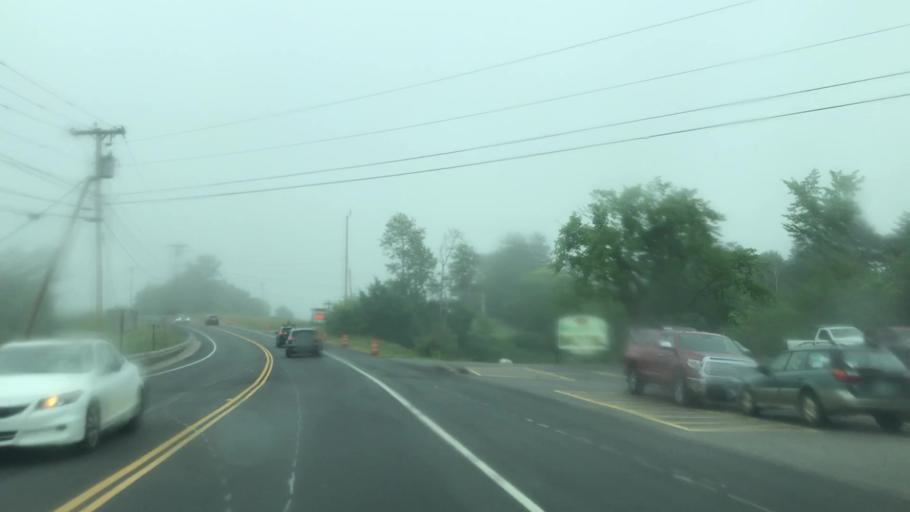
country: US
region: Maine
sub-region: Lincoln County
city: Waldoboro
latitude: 44.1036
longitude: -69.3678
